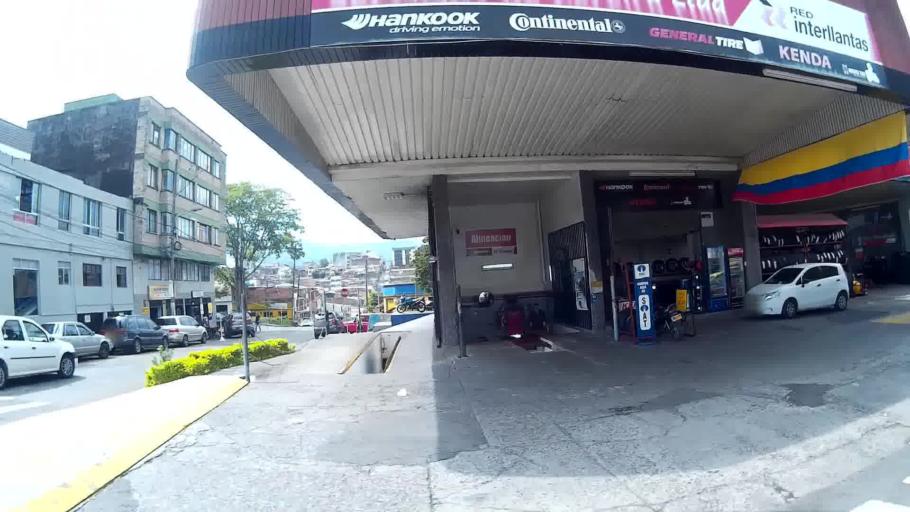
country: CO
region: Risaralda
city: Pereira
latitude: 4.8106
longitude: -75.7016
